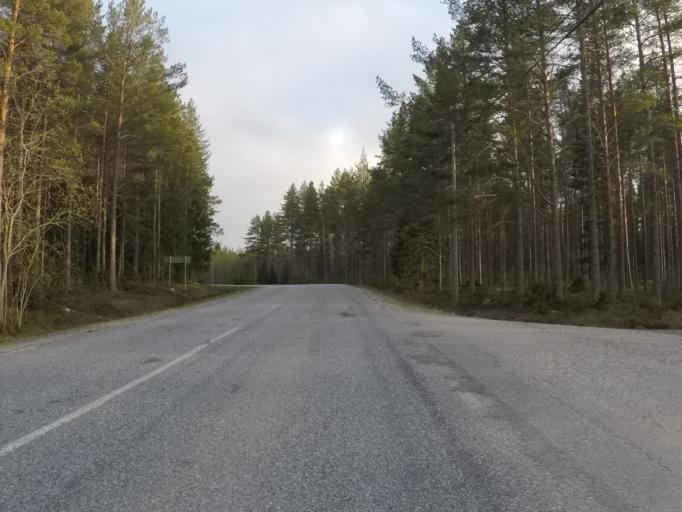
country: SE
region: Vaesterbotten
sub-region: Robertsfors Kommun
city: Robertsfors
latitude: 63.9641
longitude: 20.8095
